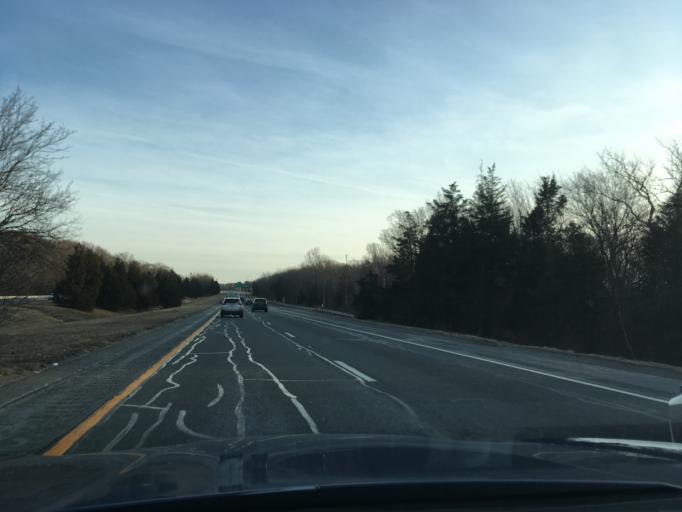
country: US
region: Rhode Island
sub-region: Providence County
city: Johnston
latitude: 41.7968
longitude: -71.5098
